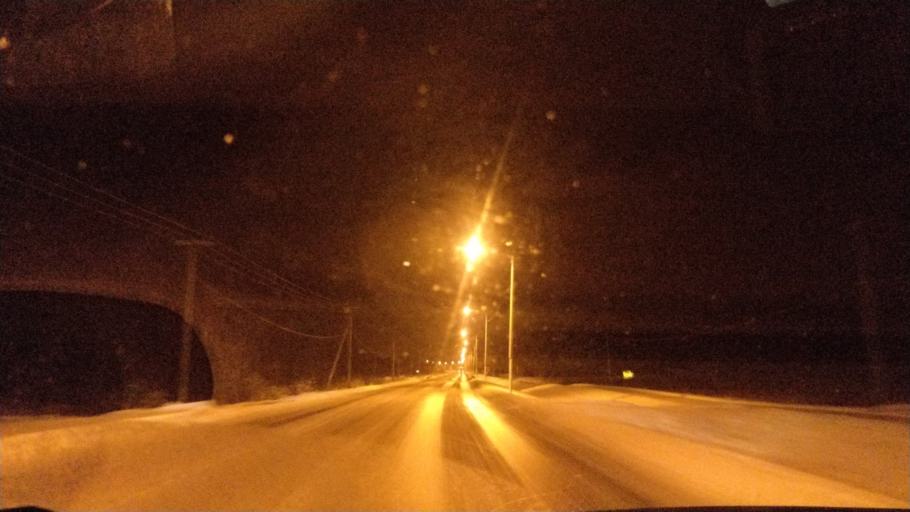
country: FI
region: Lapland
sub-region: Rovaniemi
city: Rovaniemi
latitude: 66.3089
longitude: 25.3607
